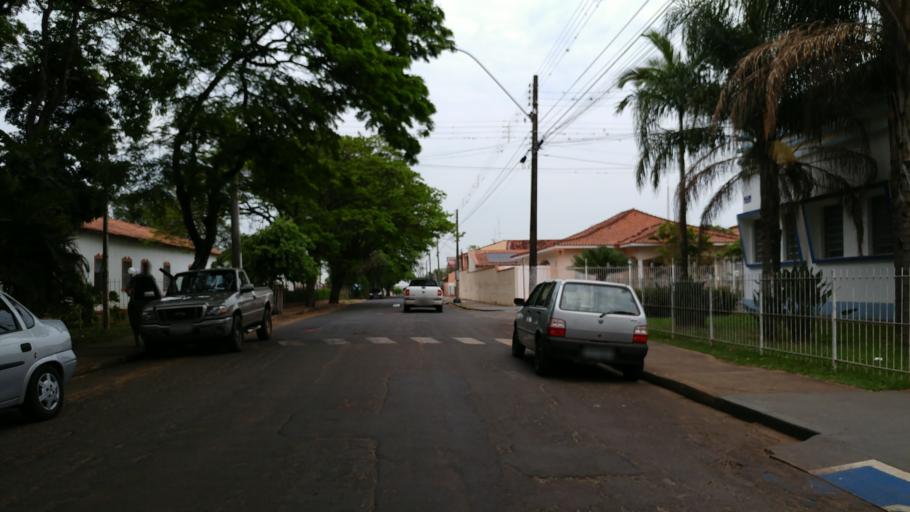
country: BR
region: Sao Paulo
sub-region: Paraguacu Paulista
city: Paraguacu Paulista
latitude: -22.4153
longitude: -50.5817
